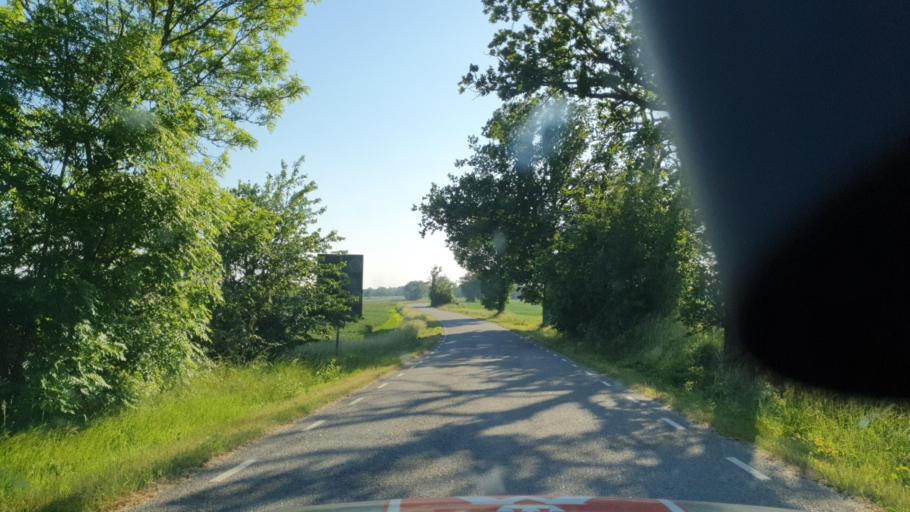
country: SE
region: Kalmar
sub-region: Kalmar Kommun
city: Ljungbyholm
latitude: 56.5012
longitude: 16.1371
